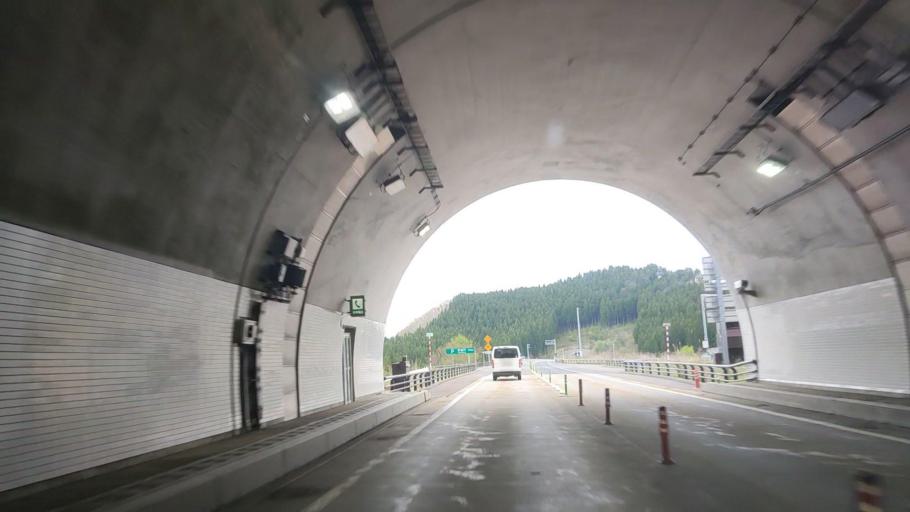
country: JP
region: Akita
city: Odate
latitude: 40.3285
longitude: 140.6067
